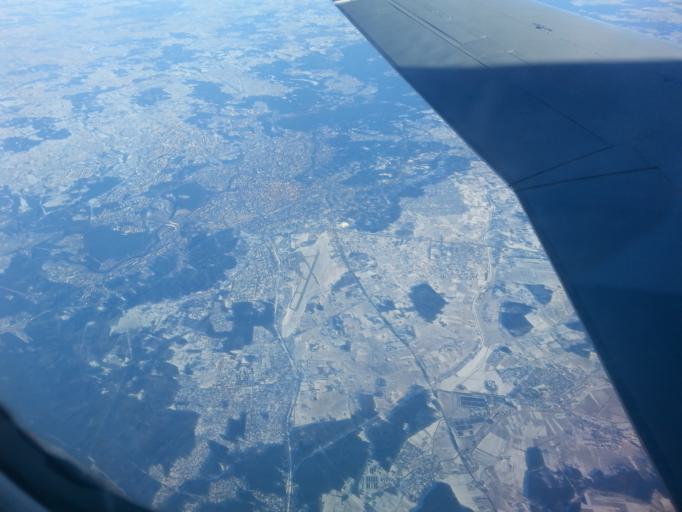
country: LT
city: Baltoji Voke
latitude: 54.5332
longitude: 25.2622
